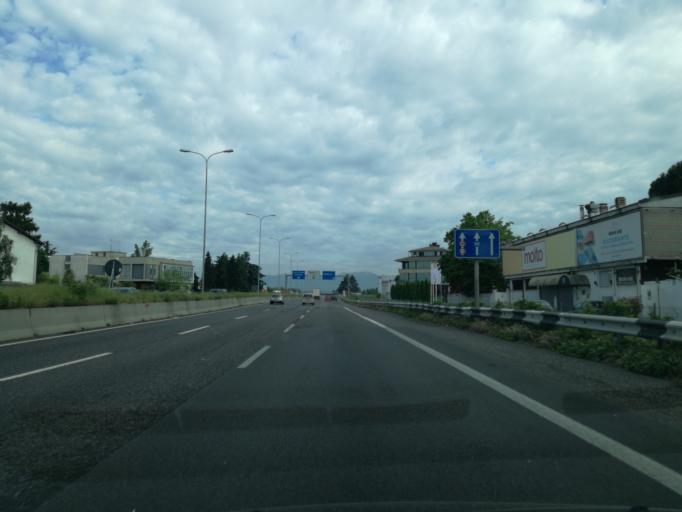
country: IT
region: Lombardy
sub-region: Provincia di Monza e Brianza
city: Carate Brianza
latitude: 45.6567
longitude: 9.2259
